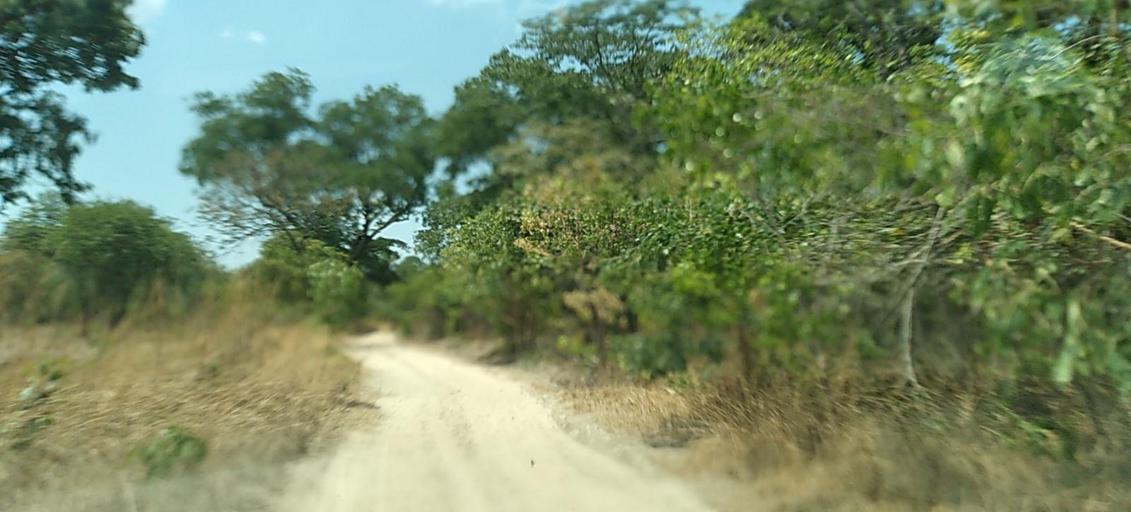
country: ZM
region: Central
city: Kapiri Mposhi
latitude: -13.6658
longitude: 28.4918
